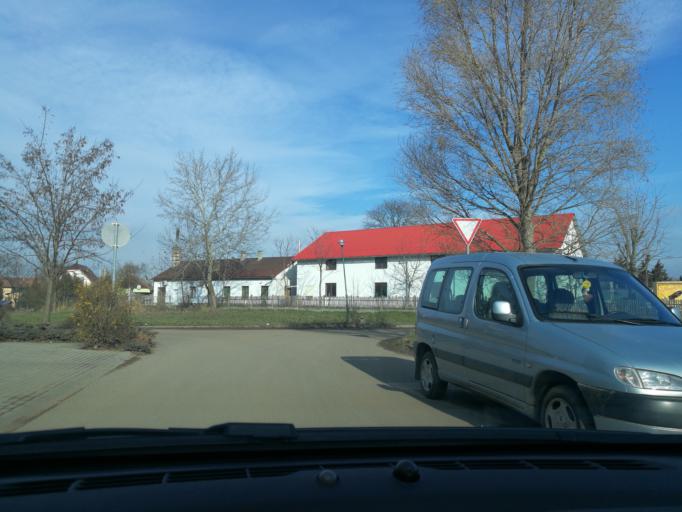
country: HU
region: Szabolcs-Szatmar-Bereg
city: Nyiregyhaza
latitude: 47.9642
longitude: 21.7324
